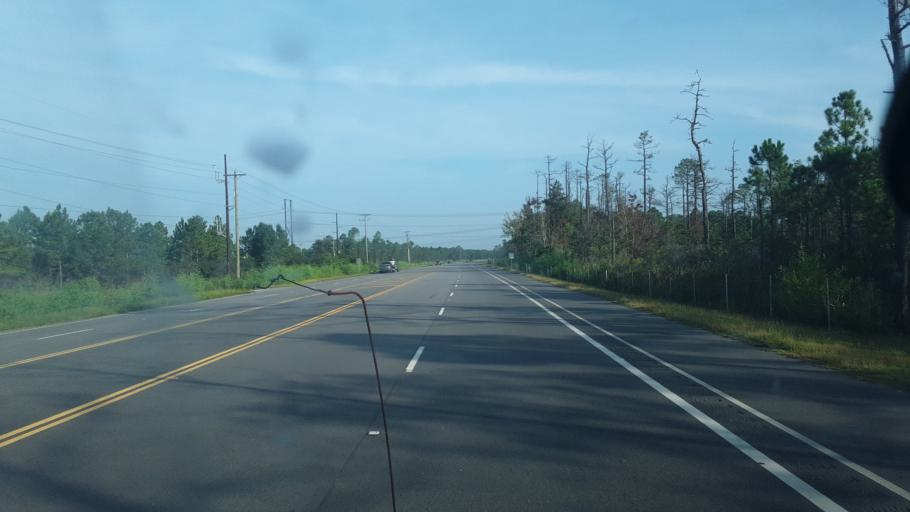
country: US
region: South Carolina
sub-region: Horry County
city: Myrtle Beach
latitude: 33.7842
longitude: -78.8767
